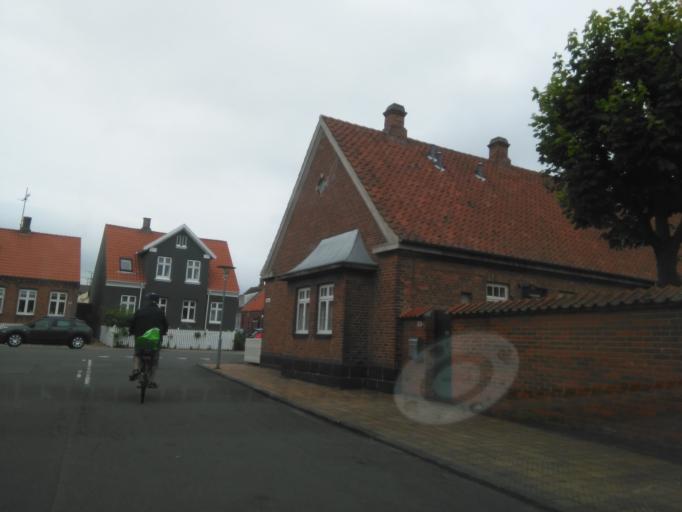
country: DK
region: Capital Region
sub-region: Bornholm Kommune
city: Ronne
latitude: 55.0964
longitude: 14.7019
